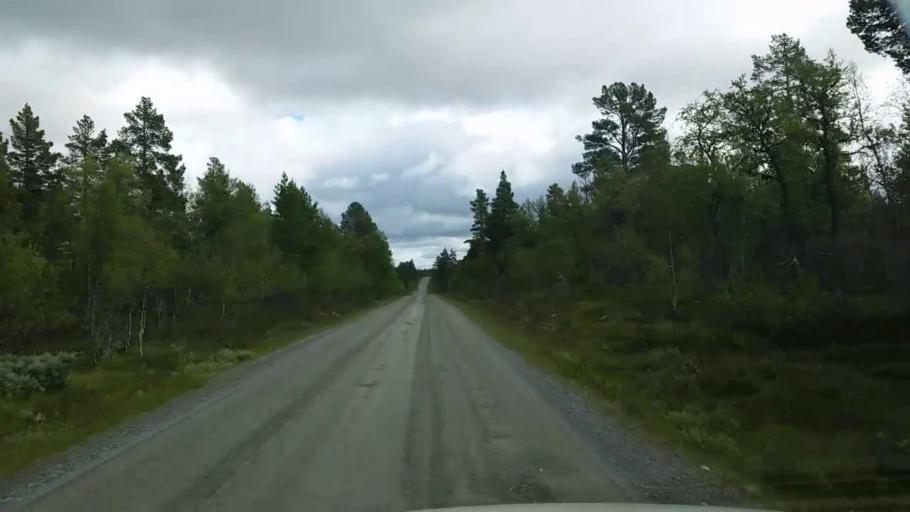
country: NO
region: Hedmark
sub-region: Engerdal
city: Engerdal
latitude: 62.3480
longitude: 12.5821
